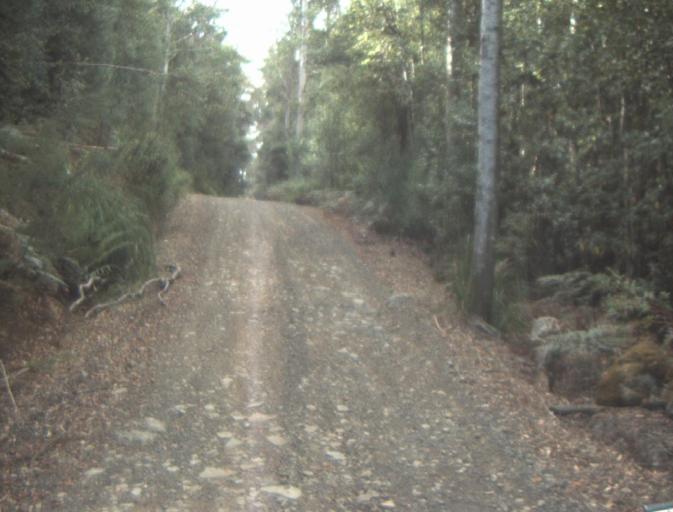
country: AU
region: Tasmania
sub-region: Launceston
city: Mayfield
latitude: -41.2868
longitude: 147.2365
